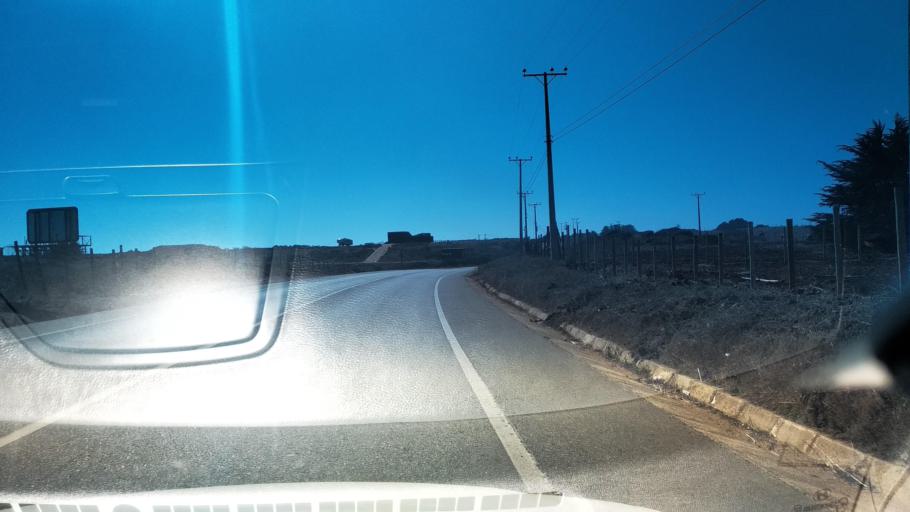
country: CL
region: O'Higgins
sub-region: Provincia de Colchagua
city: Santa Cruz
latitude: -34.4477
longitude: -72.0316
